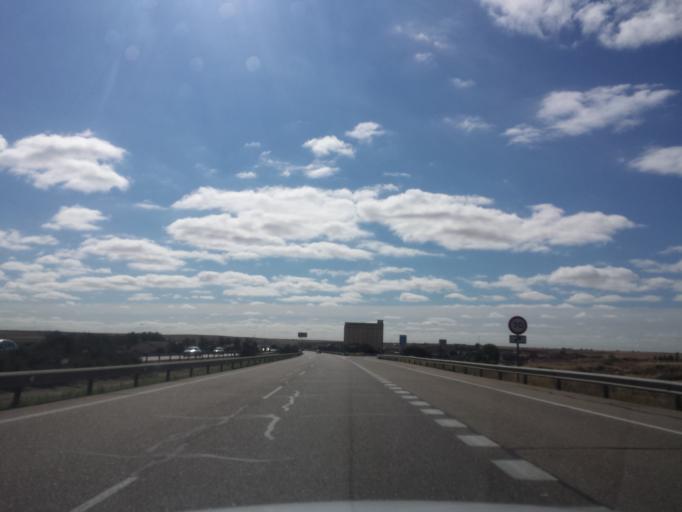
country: ES
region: Castille and Leon
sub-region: Provincia de Zamora
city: Cerecinos de Campos
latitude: 41.9068
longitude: -5.4953
